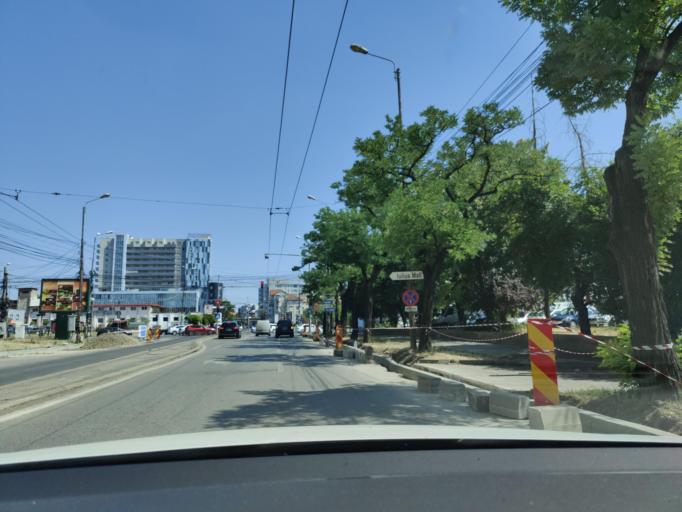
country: RO
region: Timis
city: Timisoara
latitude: 45.7604
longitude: 21.2174
